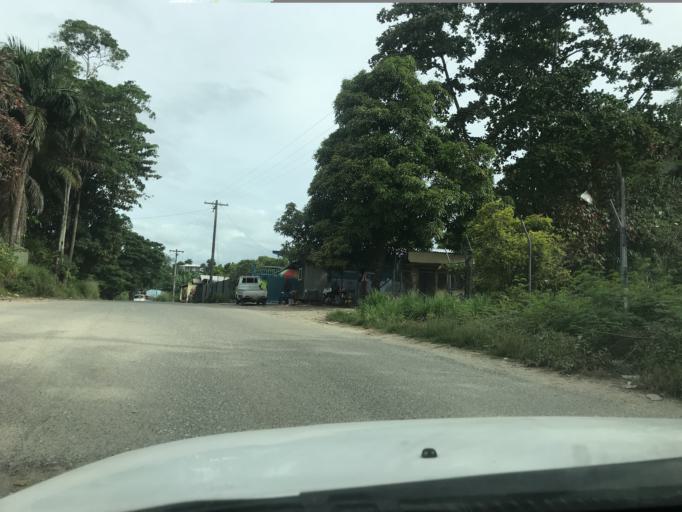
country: SB
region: Guadalcanal
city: Honiara
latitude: -9.4324
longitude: 159.9446
